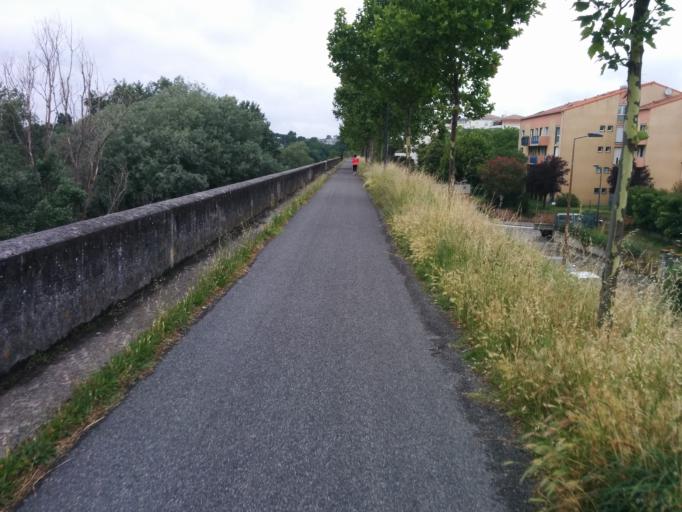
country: FR
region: Midi-Pyrenees
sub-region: Departement de la Haute-Garonne
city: Blagnac
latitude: 43.6135
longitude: 1.4076
